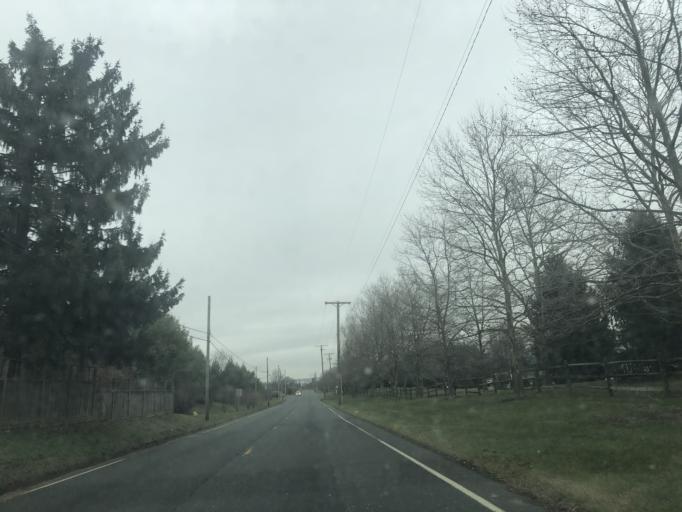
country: US
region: New Jersey
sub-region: Monmouth County
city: Allentown
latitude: 40.1974
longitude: -74.5881
